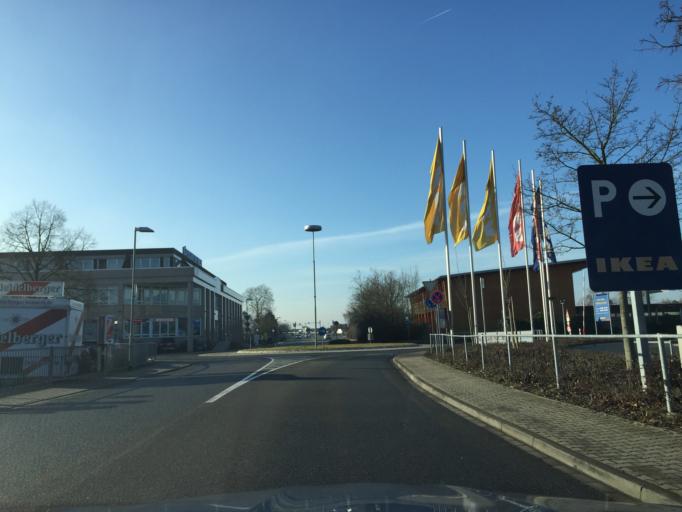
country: DE
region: Baden-Wuerttemberg
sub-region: Karlsruhe Region
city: Walldorf
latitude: 49.3052
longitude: 8.6304
